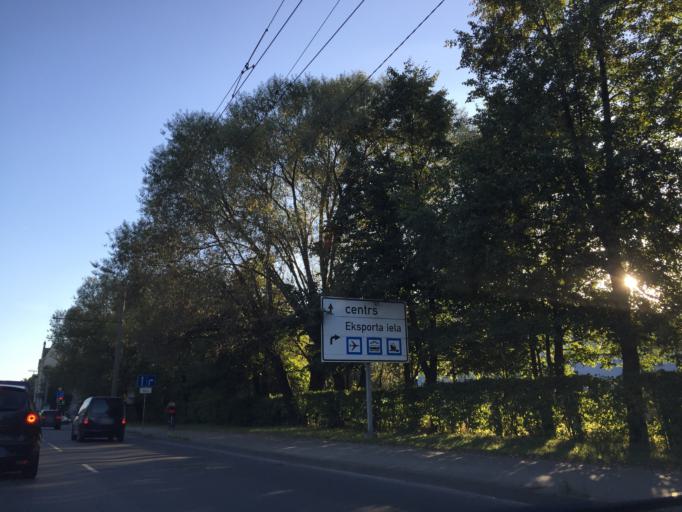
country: LV
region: Riga
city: Riga
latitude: 56.9754
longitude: 24.1123
